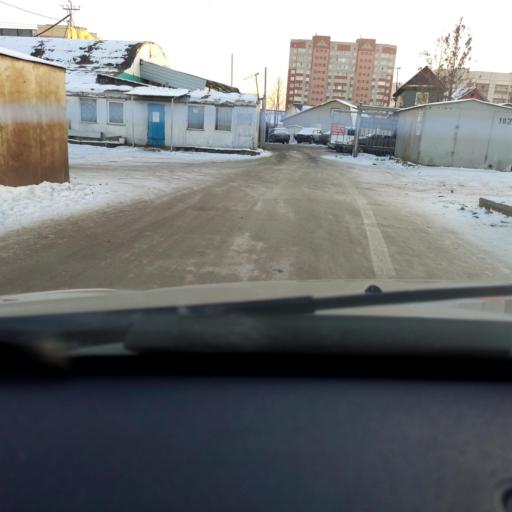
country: RU
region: Bashkortostan
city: Mikhaylovka
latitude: 54.7157
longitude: 55.8287
